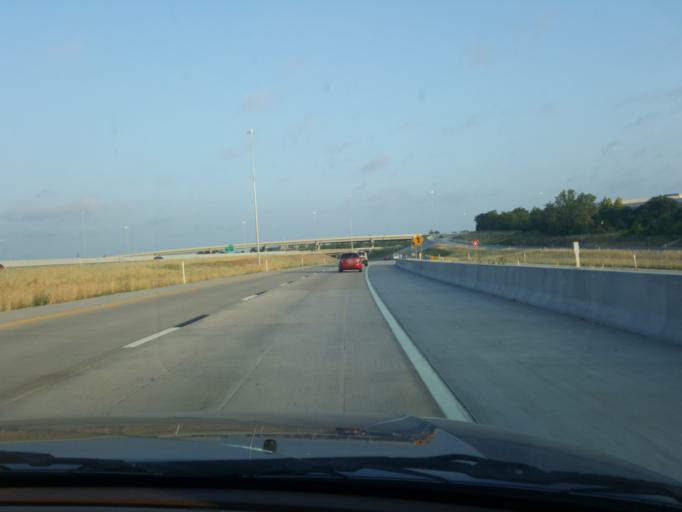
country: US
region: Kansas
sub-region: Johnson County
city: Lenexa
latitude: 38.9435
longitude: -94.7662
